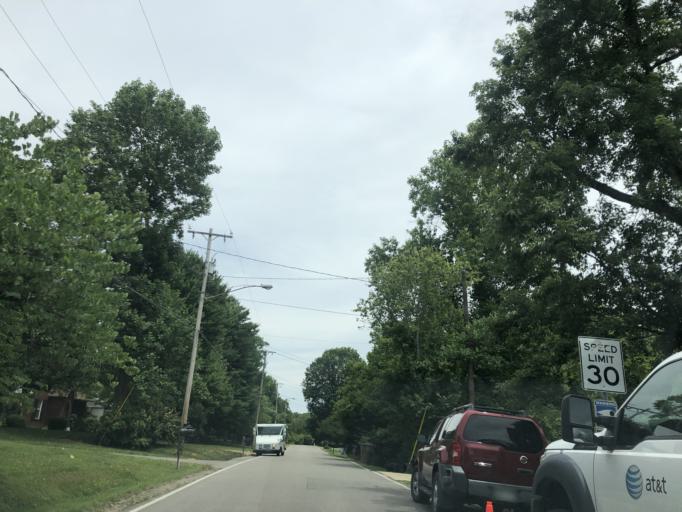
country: US
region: Tennessee
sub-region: Davidson County
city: Oak Hill
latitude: 36.1092
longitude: -86.7921
